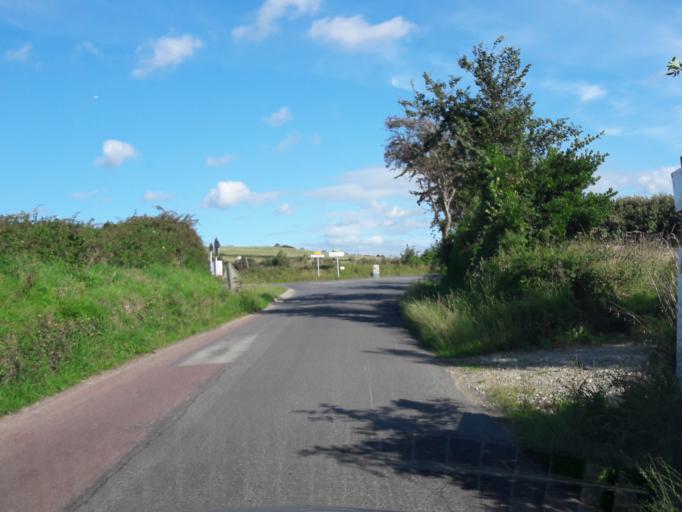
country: FR
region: Lower Normandy
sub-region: Departement de la Manche
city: Les Pieux
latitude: 49.4948
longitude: -1.8300
